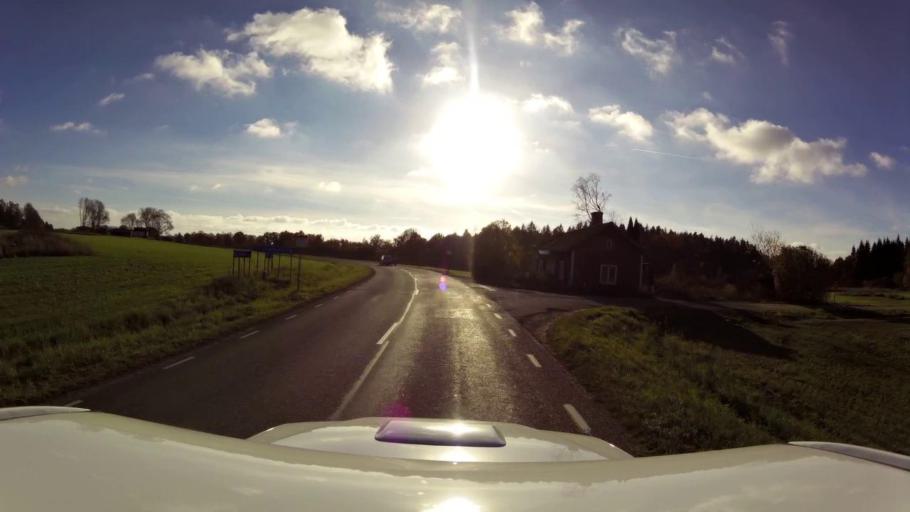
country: SE
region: OEstergoetland
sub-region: Linkopings Kommun
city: Malmslatt
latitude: 58.3371
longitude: 15.5129
